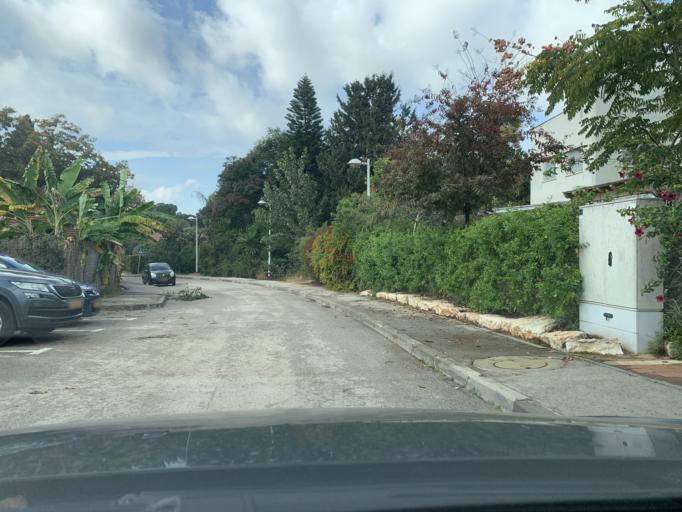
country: PS
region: West Bank
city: Qalqilyah
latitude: 32.1989
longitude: 34.9509
